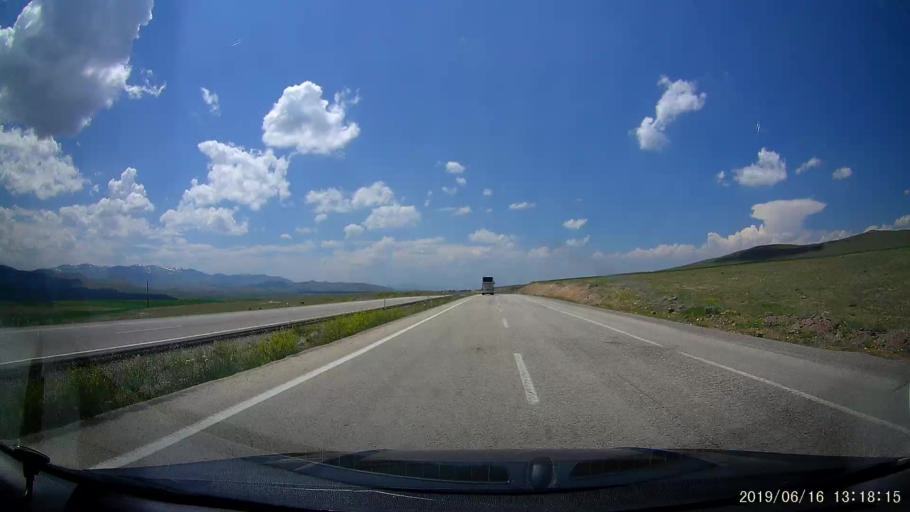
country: TR
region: Agri
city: Taslicay
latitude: 39.6298
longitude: 43.4347
